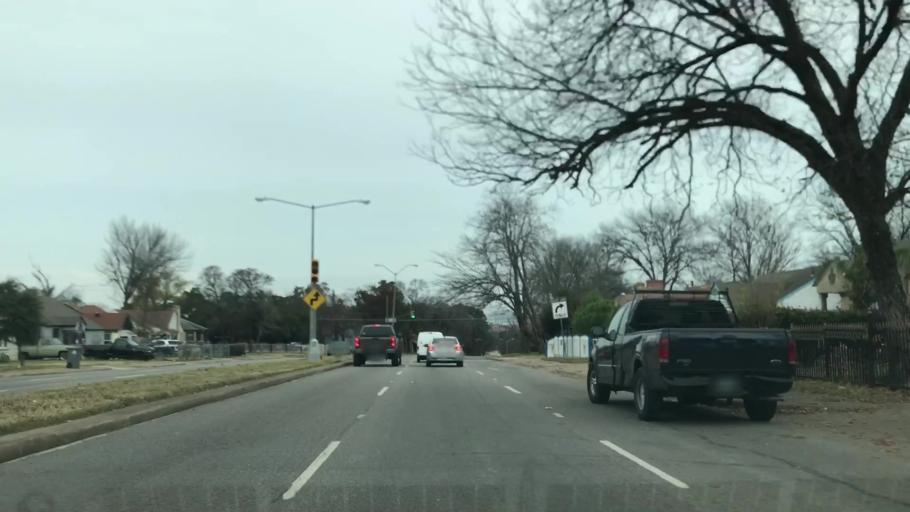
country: US
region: Texas
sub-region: Dallas County
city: Dallas
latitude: 32.7320
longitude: -96.8143
